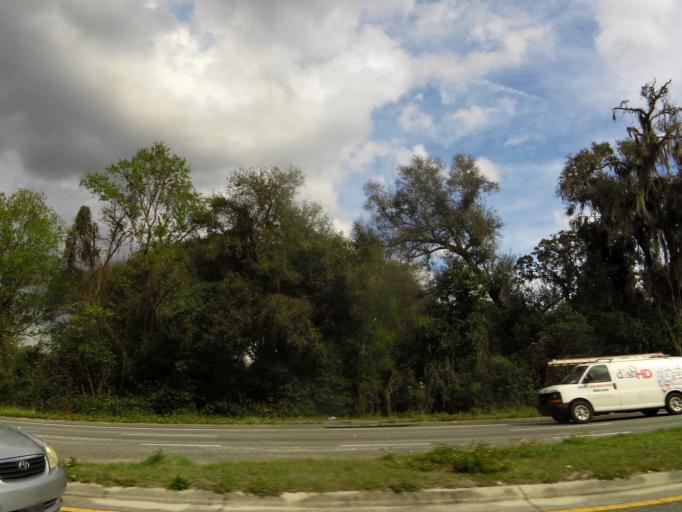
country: US
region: Florida
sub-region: Volusia County
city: North DeLand
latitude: 29.0758
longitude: -81.3255
